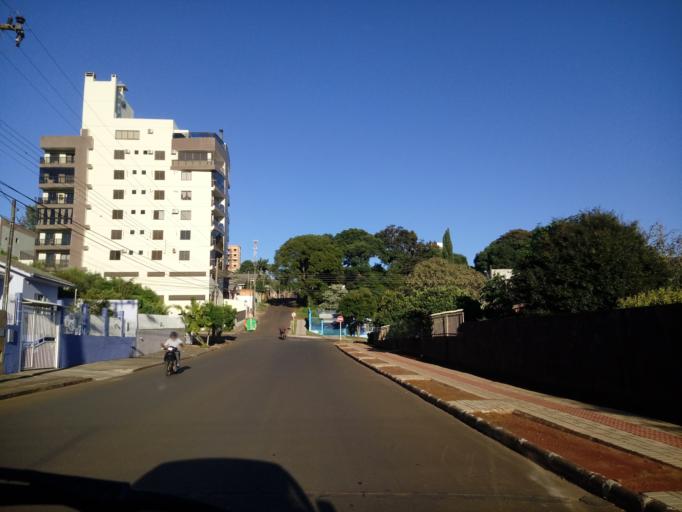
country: BR
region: Santa Catarina
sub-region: Chapeco
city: Chapeco
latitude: -27.1127
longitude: -52.6064
